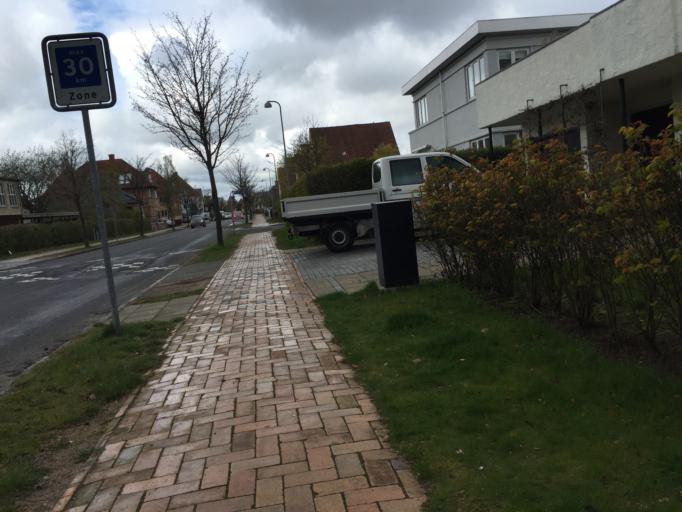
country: DK
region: South Denmark
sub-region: Odense Kommune
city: Odense
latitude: 55.3869
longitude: 10.3993
